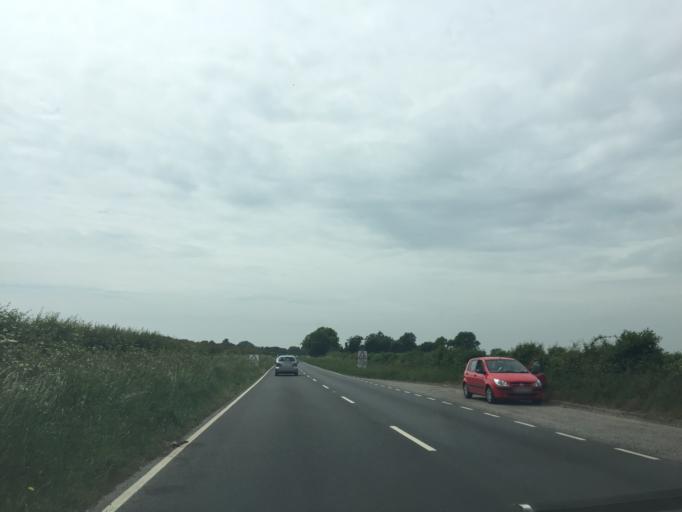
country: GB
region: England
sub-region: Dorset
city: Bovington Camp
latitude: 50.6633
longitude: -2.3126
